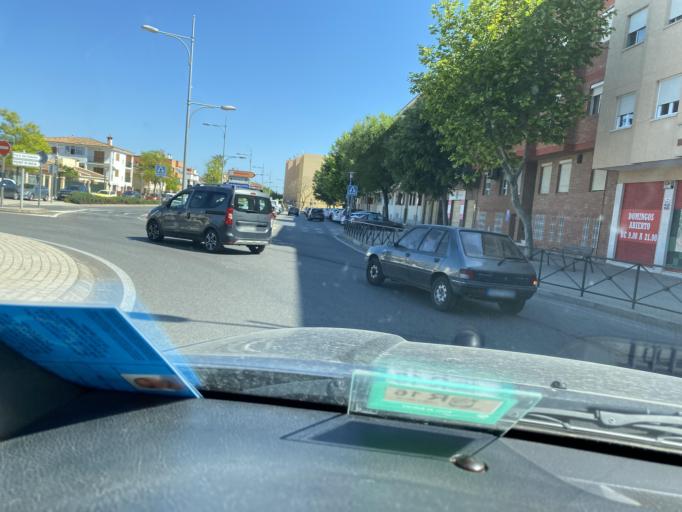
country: ES
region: Balearic Islands
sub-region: Illes Balears
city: Palma
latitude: 39.6032
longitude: 2.6875
